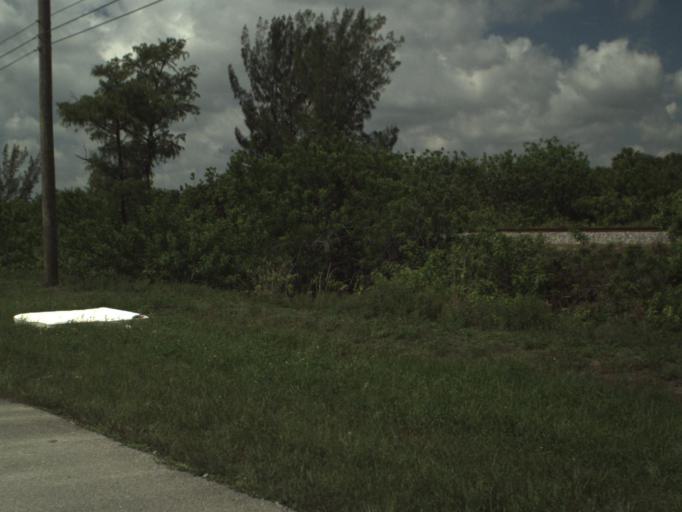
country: US
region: Florida
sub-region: Palm Beach County
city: Juno Beach
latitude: 26.8622
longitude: -80.0961
